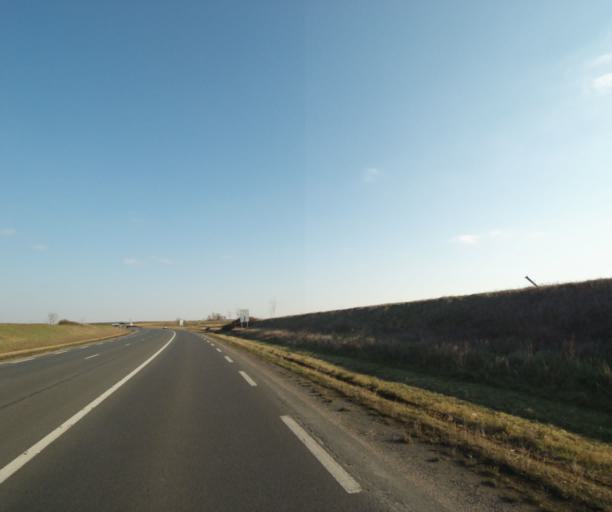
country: FR
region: Poitou-Charentes
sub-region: Departement des Deux-Sevres
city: Vouille
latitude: 46.3112
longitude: -0.3794
